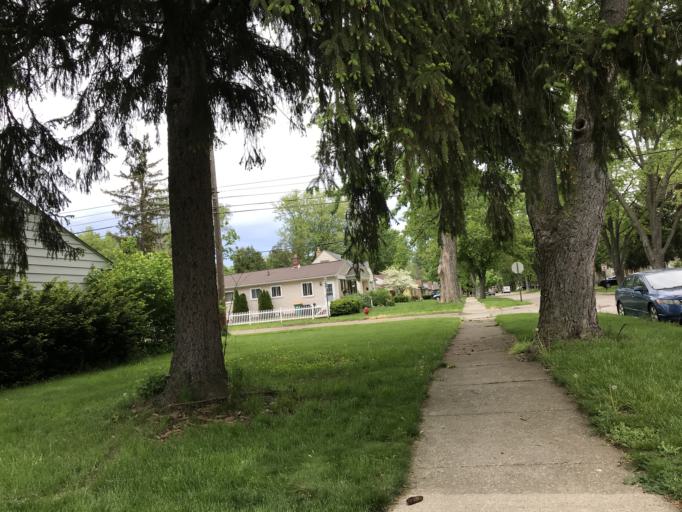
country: US
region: Michigan
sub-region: Oakland County
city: Farmington
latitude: 42.4594
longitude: -83.3542
